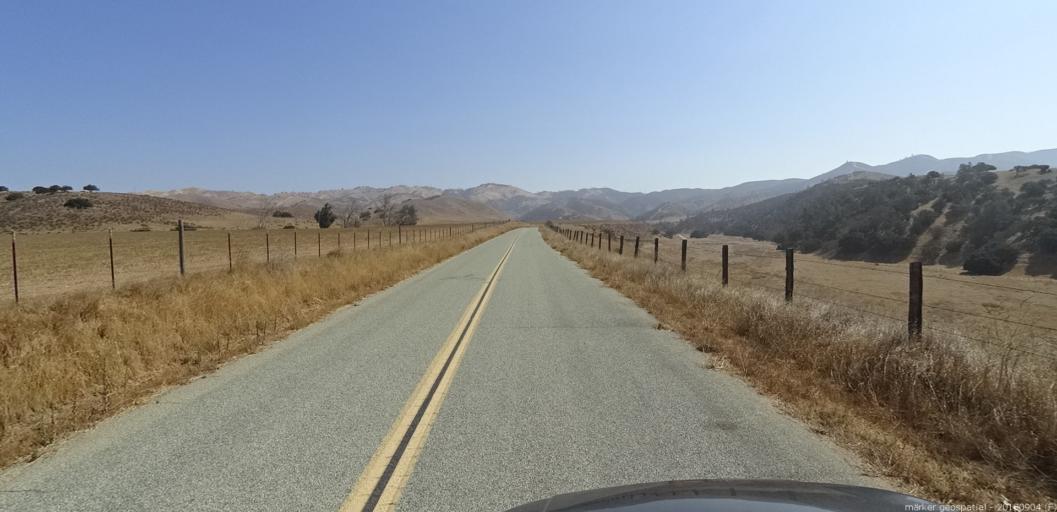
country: US
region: California
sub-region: Monterey County
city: Gonzales
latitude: 36.5112
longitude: -121.3553
